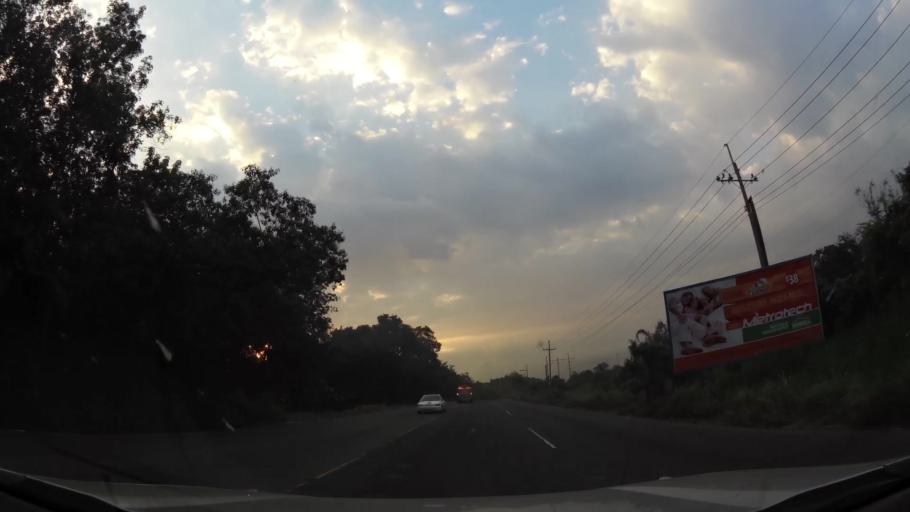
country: GT
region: Escuintla
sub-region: Municipio de La Democracia
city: La Democracia
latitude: 14.2713
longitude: -90.9018
